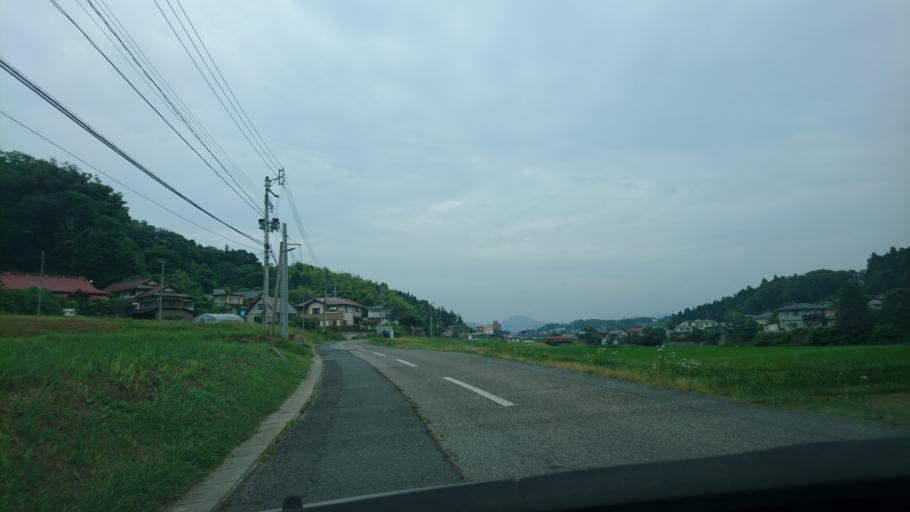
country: JP
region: Iwate
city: Ichinoseki
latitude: 38.9120
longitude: 141.1228
